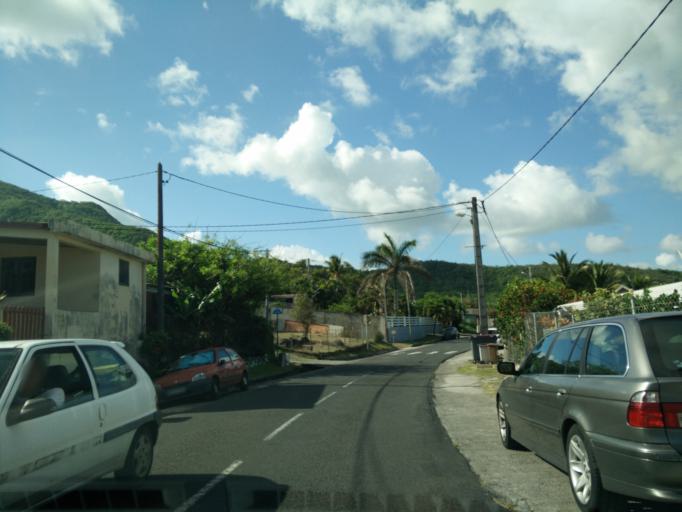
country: MQ
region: Martinique
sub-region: Martinique
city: Les Trois-Ilets
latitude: 14.4670
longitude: -61.0471
